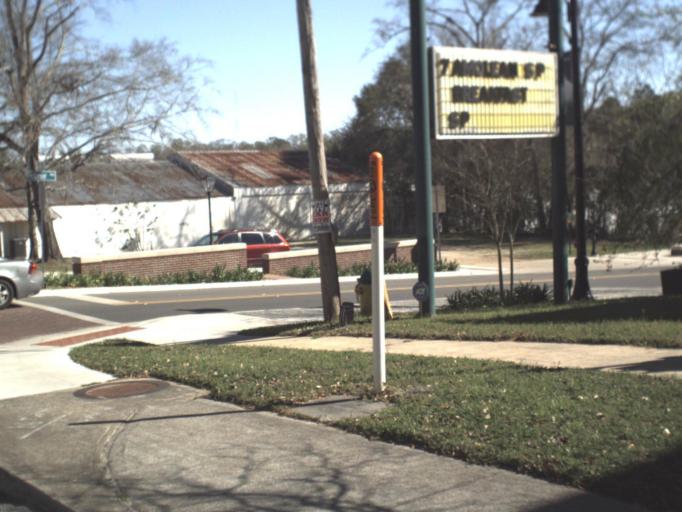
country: US
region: Florida
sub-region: Leon County
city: Tallahassee
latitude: 30.4270
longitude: -84.2819
